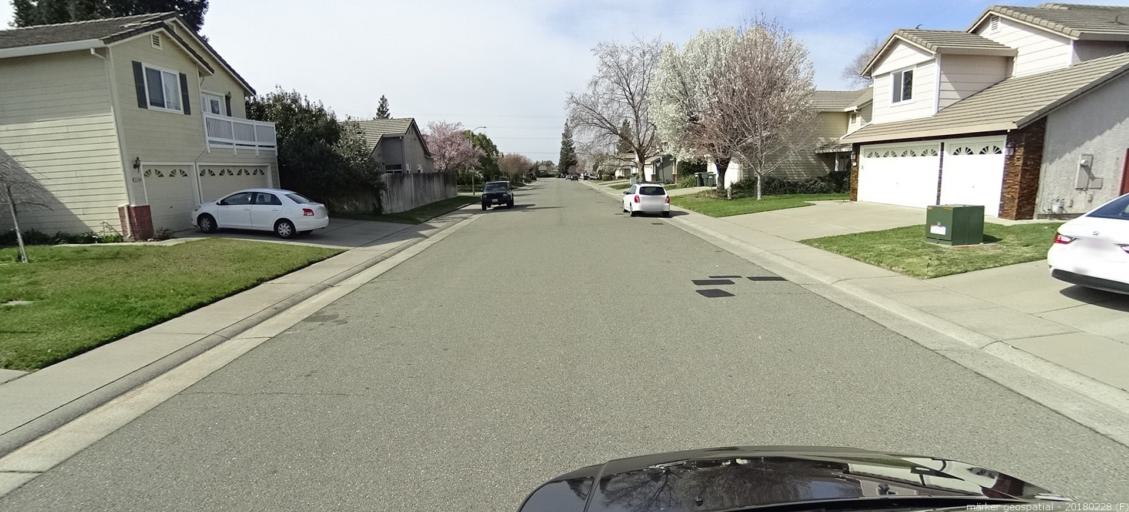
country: US
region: California
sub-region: Sacramento County
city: Antelope
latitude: 38.7248
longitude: -121.3437
